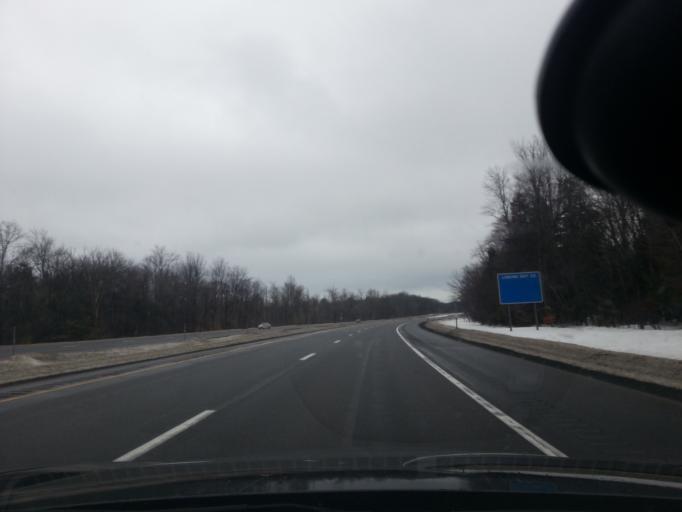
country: US
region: New York
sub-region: Oswego County
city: Central Square
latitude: 43.3013
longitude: -76.1252
